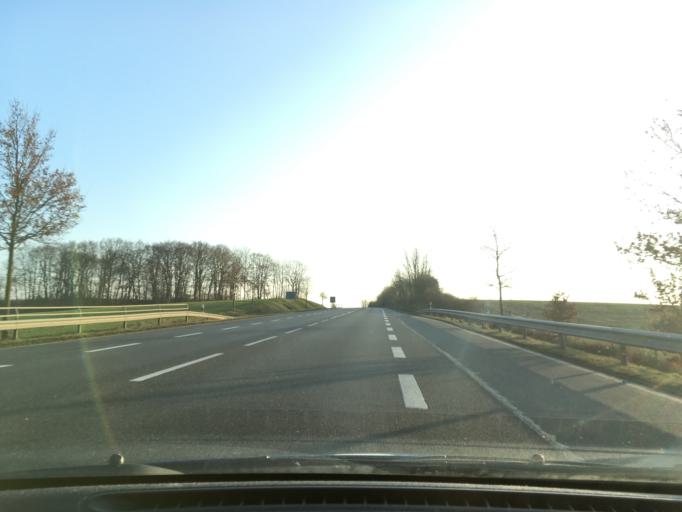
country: DE
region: Lower Saxony
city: Barum
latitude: 53.0604
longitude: 10.5348
